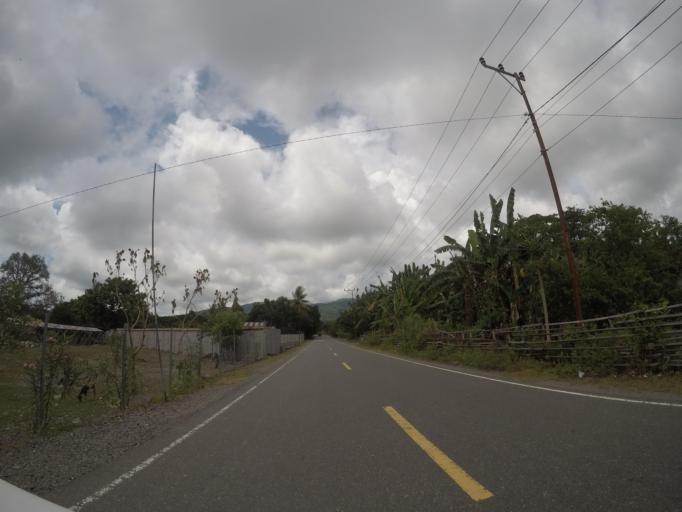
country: TL
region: Liquica
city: Maubara
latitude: -8.7337
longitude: 125.1362
